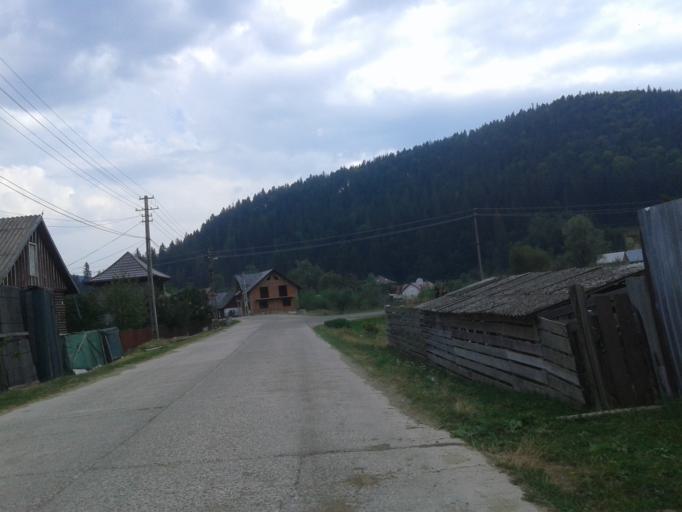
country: RO
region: Suceava
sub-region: Comuna Putna
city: Putna
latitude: 47.8655
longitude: 25.6059
